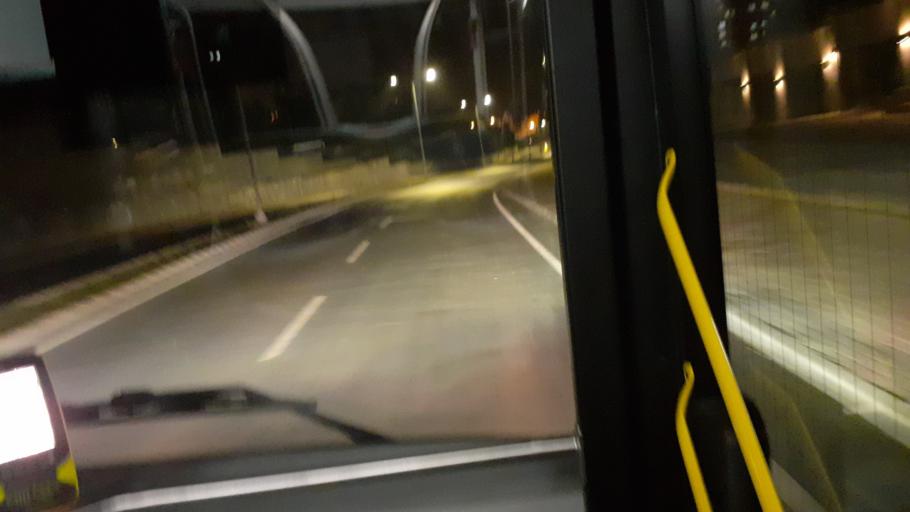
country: TR
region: Istanbul
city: Basaksehir
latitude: 41.0745
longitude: 28.7826
